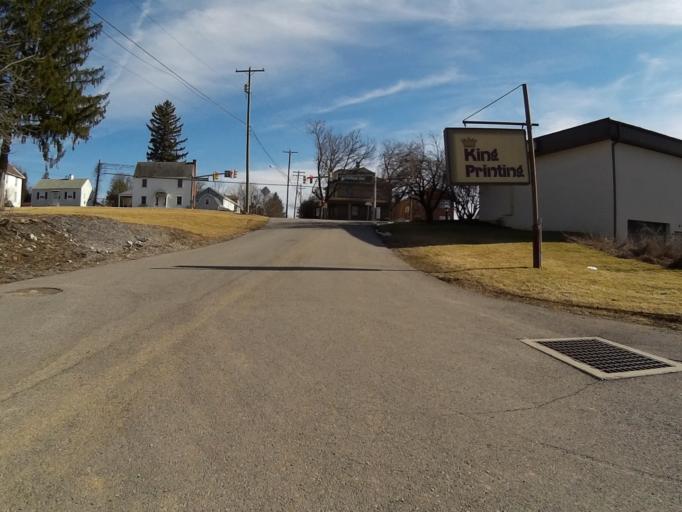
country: US
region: Pennsylvania
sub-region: Centre County
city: State College
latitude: 40.7846
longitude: -77.8752
